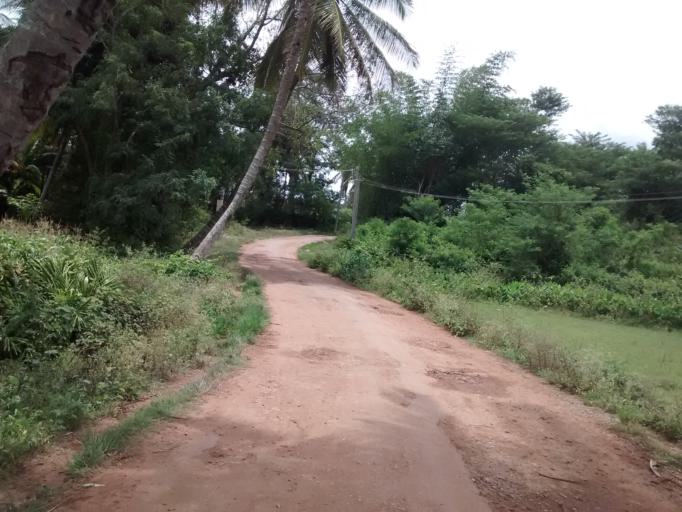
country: IN
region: Karnataka
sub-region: Hassan
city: Hassan
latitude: 12.9134
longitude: 76.1308
